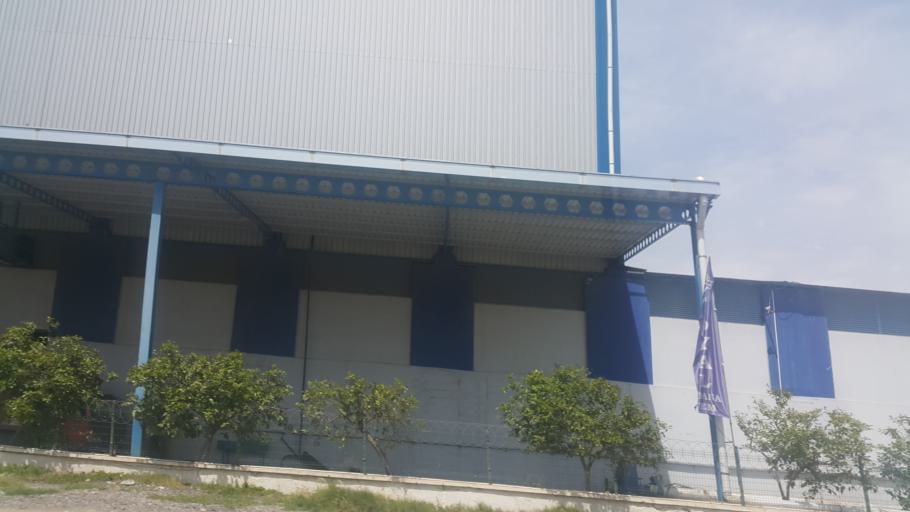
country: TR
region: Adana
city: Yakapinar
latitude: 36.9702
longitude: 35.5307
